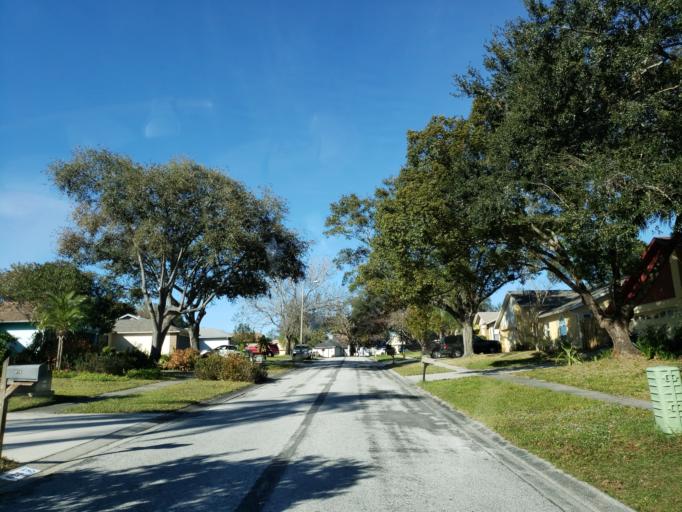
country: US
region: Florida
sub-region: Hillsborough County
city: Bloomingdale
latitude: 27.9033
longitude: -82.2738
